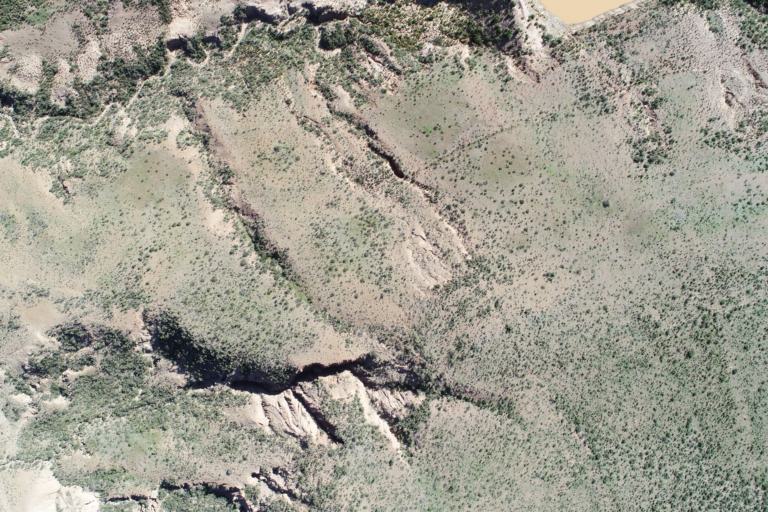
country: BO
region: La Paz
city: Curahuara de Carangas
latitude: -17.3024
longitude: -68.4879
